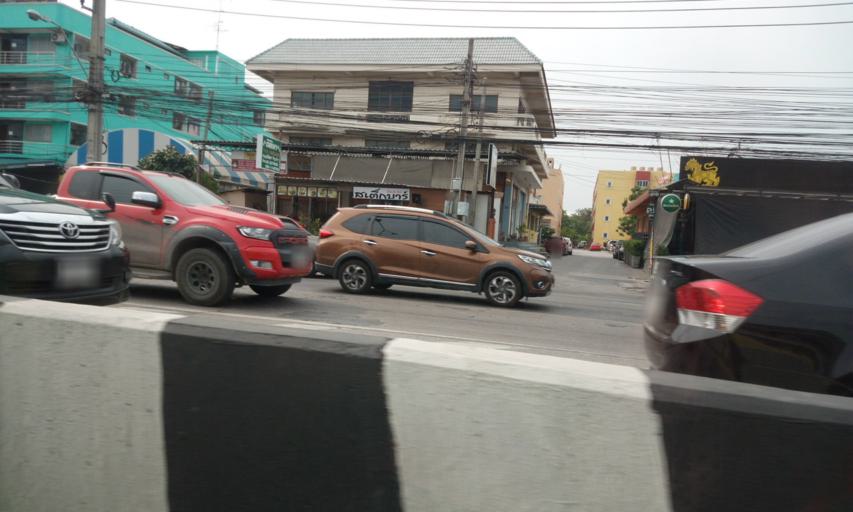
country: TH
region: Bangkok
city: Lat Krabang
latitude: 13.7218
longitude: 100.7760
